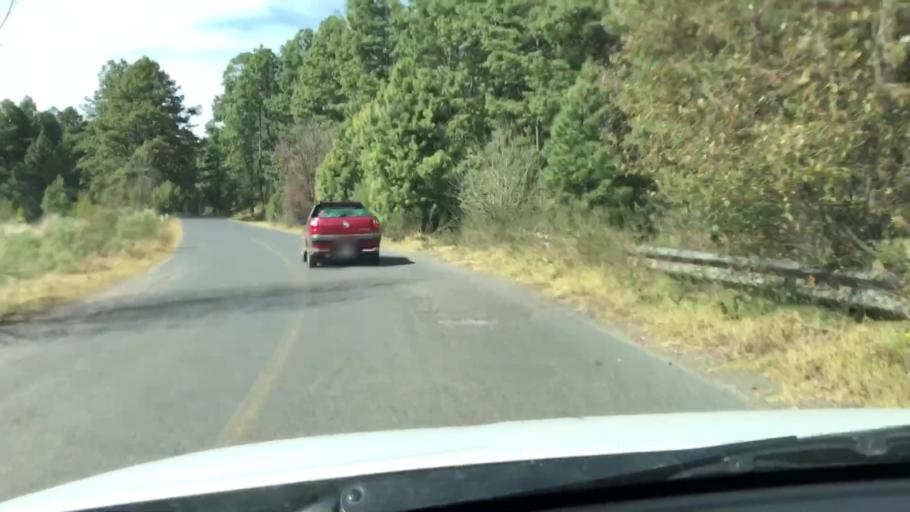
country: MX
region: Jalisco
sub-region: Amacueca
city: Tepec
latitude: 20.0522
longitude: -103.6963
